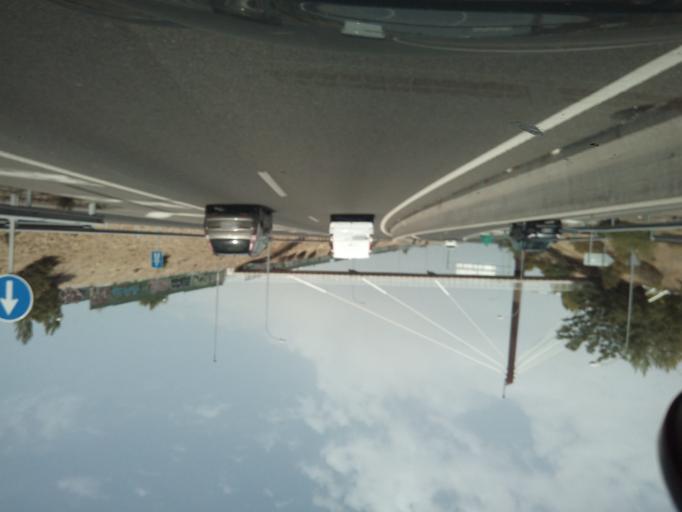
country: ES
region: Madrid
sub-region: Provincia de Madrid
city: Barajas de Madrid
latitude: 40.4685
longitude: -3.5833
